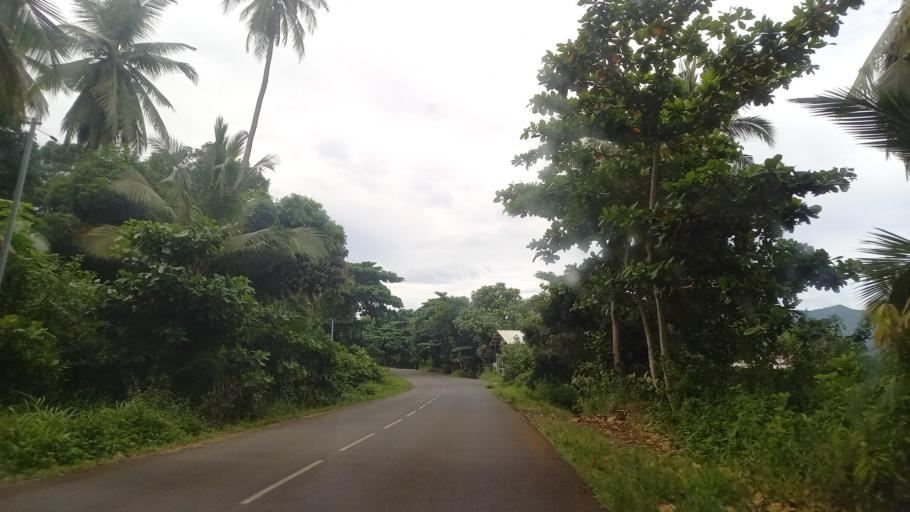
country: YT
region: Boueni
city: Boueni
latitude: -12.9170
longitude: 45.1018
